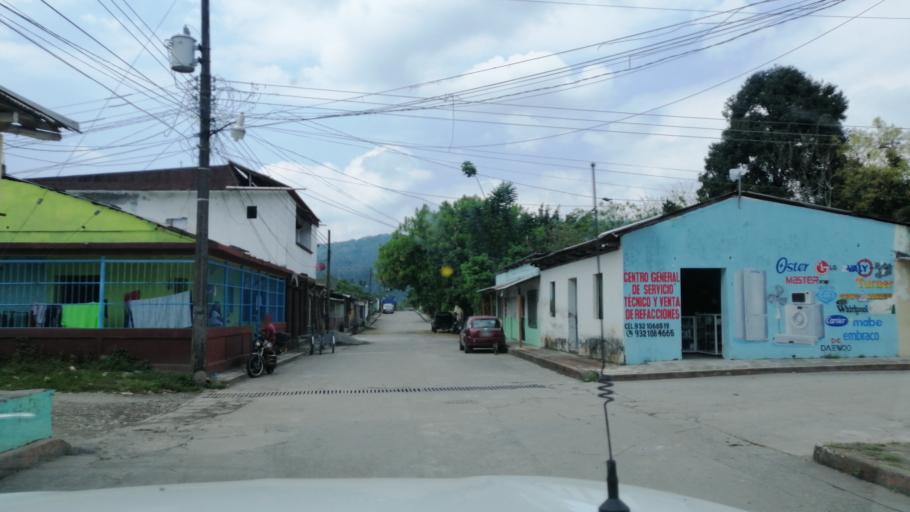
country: MX
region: Chiapas
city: Ostuacan
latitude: 17.4076
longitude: -93.3376
